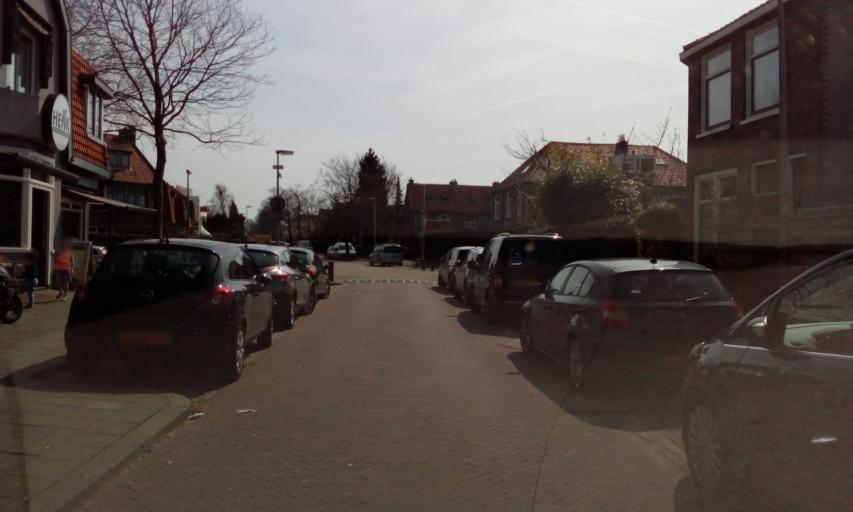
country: NL
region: North Holland
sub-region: Gemeente Bussum
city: Bussum
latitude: 52.2720
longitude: 5.1705
